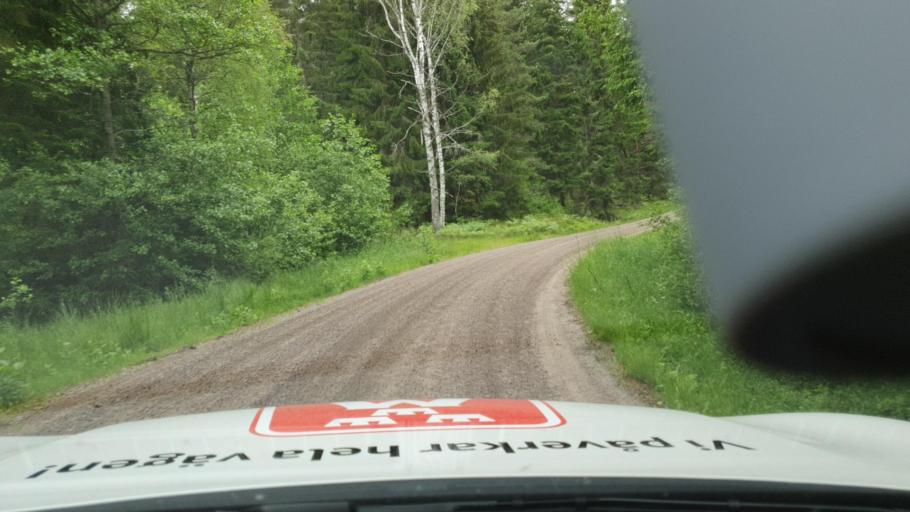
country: SE
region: Vaestra Goetaland
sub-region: Hjo Kommun
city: Hjo
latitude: 58.4051
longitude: 14.3292
